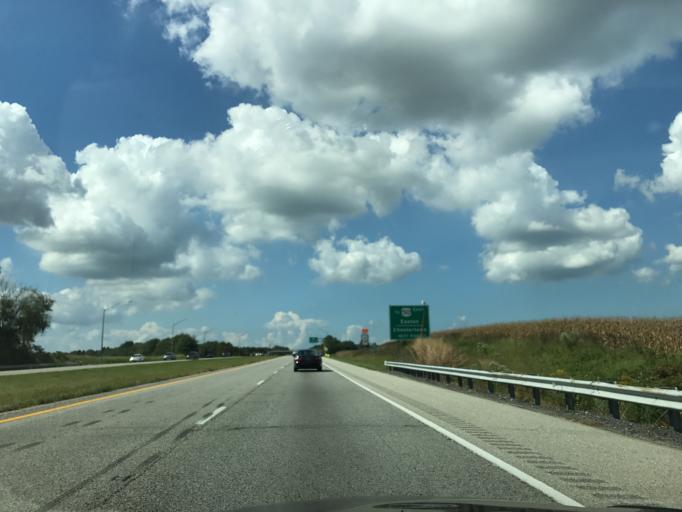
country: US
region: Maryland
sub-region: Queen Anne's County
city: Centreville
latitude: 39.0155
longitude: -76.0675
